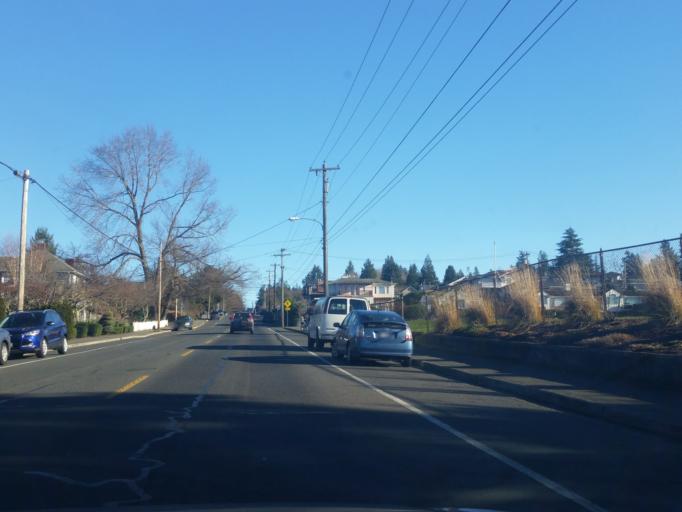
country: US
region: Washington
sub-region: Snohomish County
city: Edmonds
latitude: 47.8105
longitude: -122.3710
